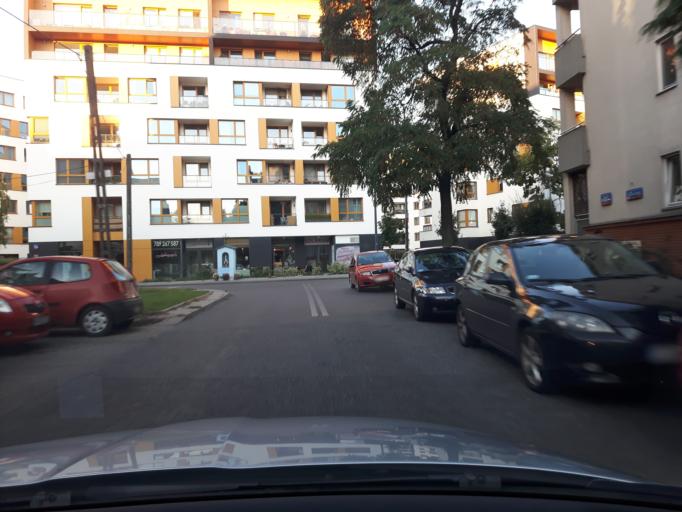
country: PL
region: Masovian Voivodeship
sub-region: Warszawa
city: Praga Poludnie
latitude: 52.2317
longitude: 21.0871
